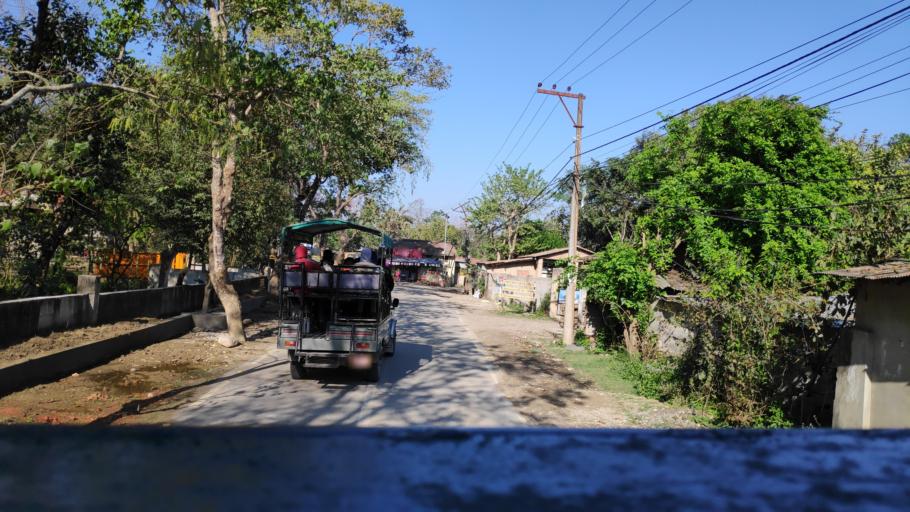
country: NP
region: Central Region
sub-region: Narayani Zone
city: Bharatpur
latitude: 27.5744
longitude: 84.4995
